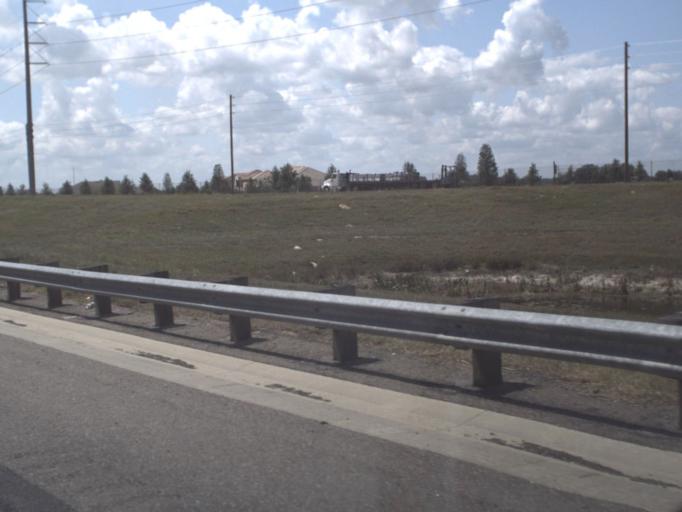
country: US
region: Florida
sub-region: Polk County
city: Citrus Ridge
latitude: 28.4326
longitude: -81.6360
